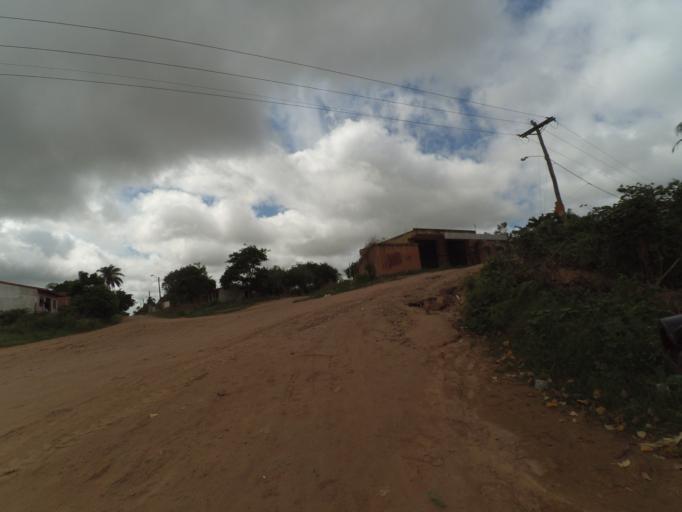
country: BO
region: Santa Cruz
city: Santa Cruz de la Sierra
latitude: -17.8765
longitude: -63.2351
